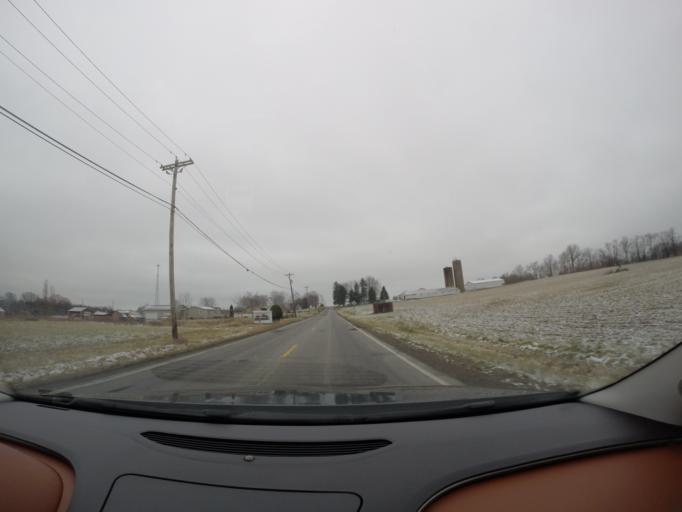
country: US
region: Ohio
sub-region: Wayne County
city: Apple Creek
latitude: 40.7961
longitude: -81.8441
